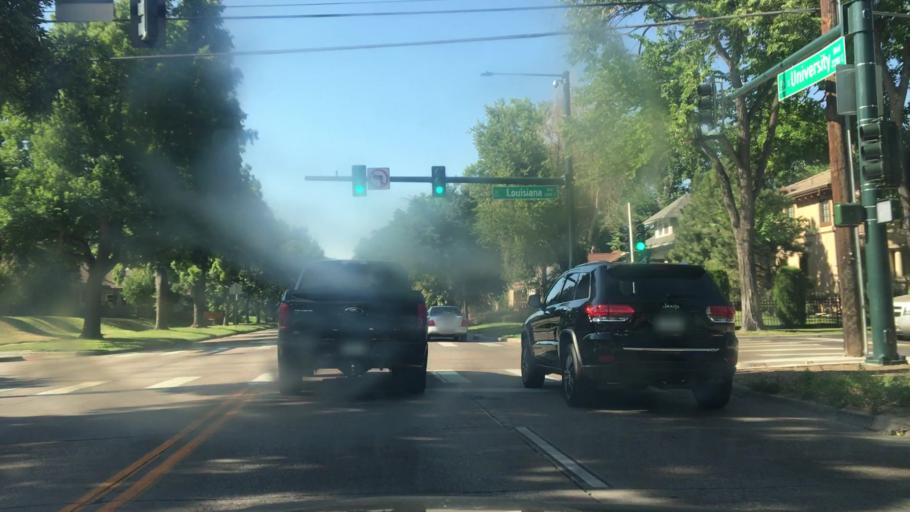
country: US
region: Colorado
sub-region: Arapahoe County
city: Glendale
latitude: 39.6931
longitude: -104.9593
